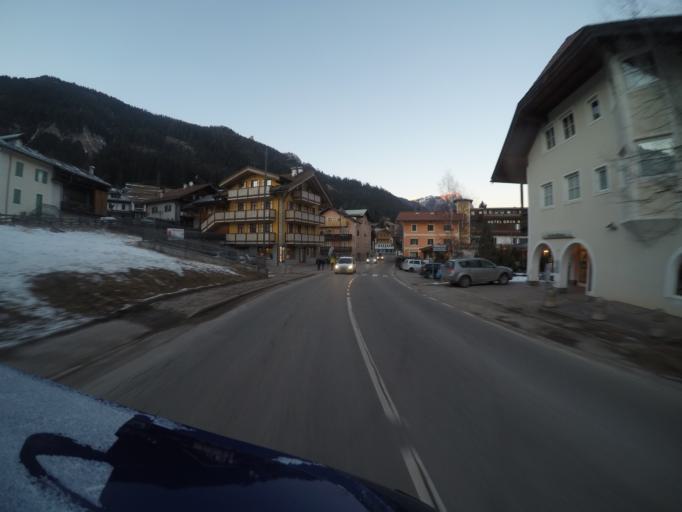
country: IT
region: Trentino-Alto Adige
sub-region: Provincia di Trento
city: Pozza di Fassa
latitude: 46.4263
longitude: 11.6827
